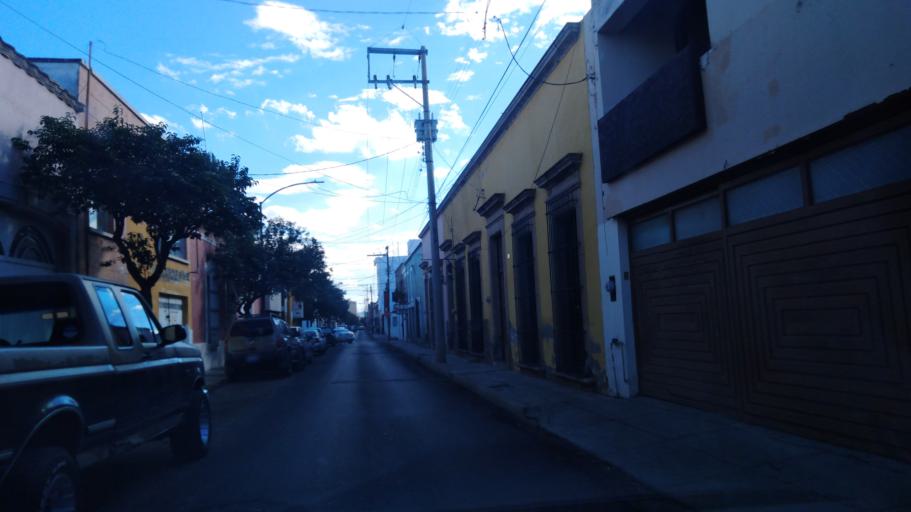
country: MX
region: Durango
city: Victoria de Durango
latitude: 24.0290
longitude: -104.6727
